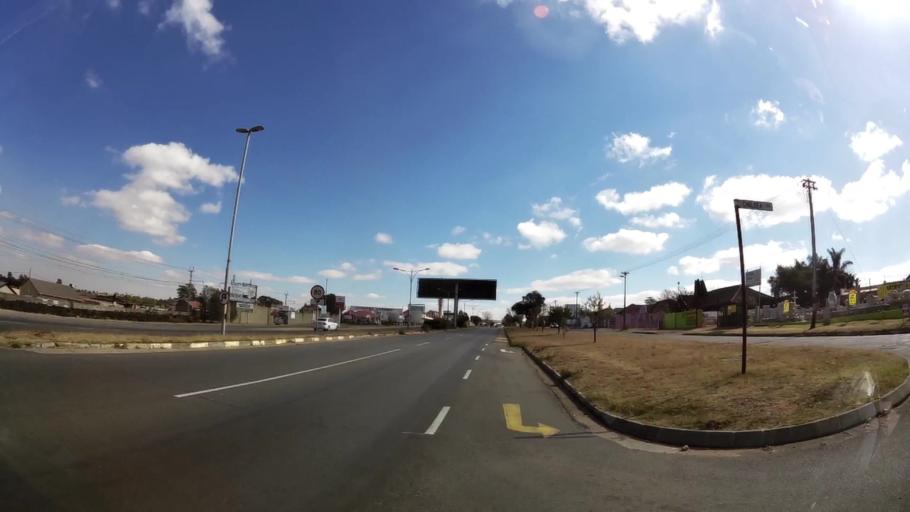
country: ZA
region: Gauteng
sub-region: West Rand District Municipality
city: Krugersdorp
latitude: -26.1232
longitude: 27.8231
